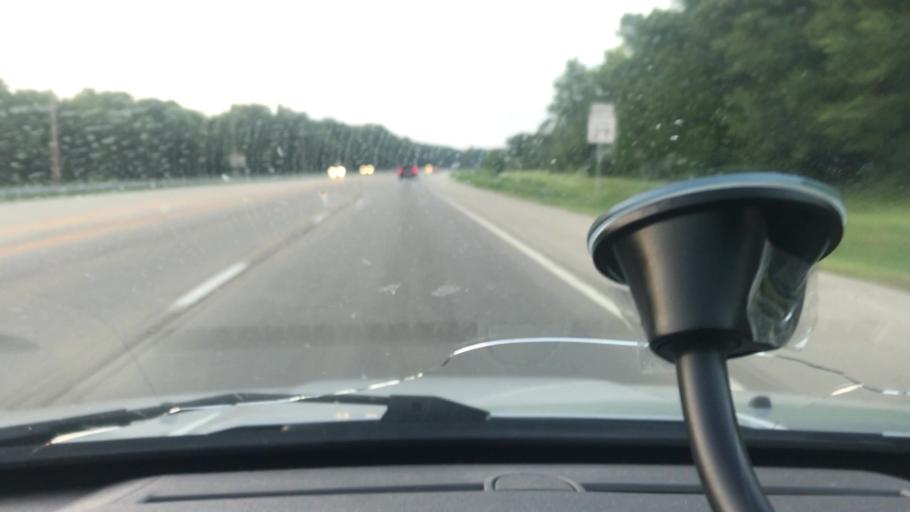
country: US
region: Illinois
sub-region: Tazewell County
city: North Pekin
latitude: 40.6052
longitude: -89.6364
